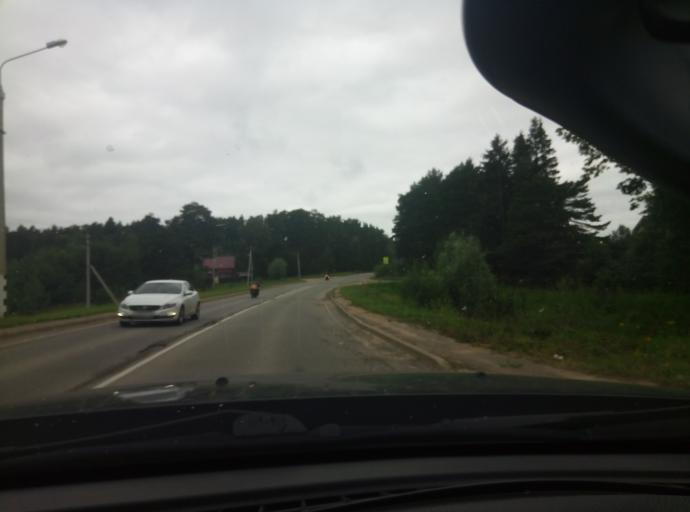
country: RU
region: Kaluga
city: Zhukovo
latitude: 54.9646
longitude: 36.7891
